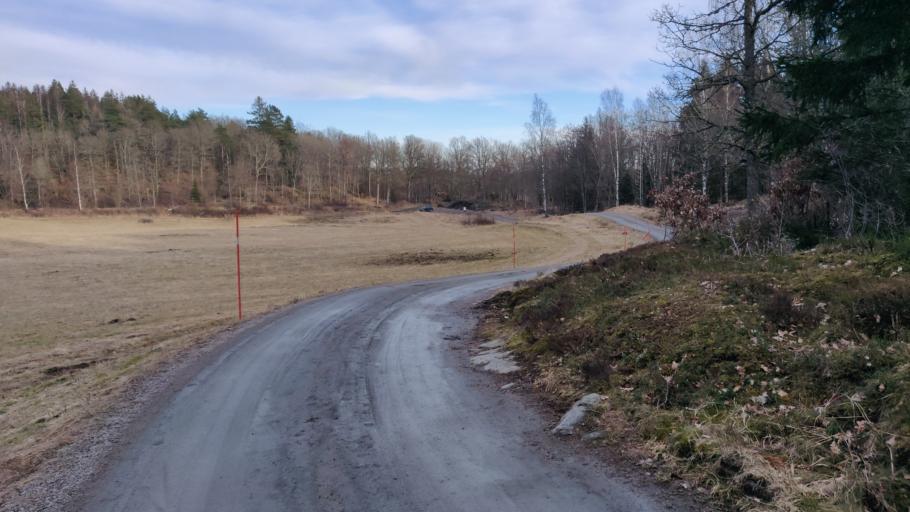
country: SE
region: Vaestra Goetaland
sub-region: Uddevalla Kommun
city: Uddevalla
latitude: 58.3694
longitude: 11.8893
